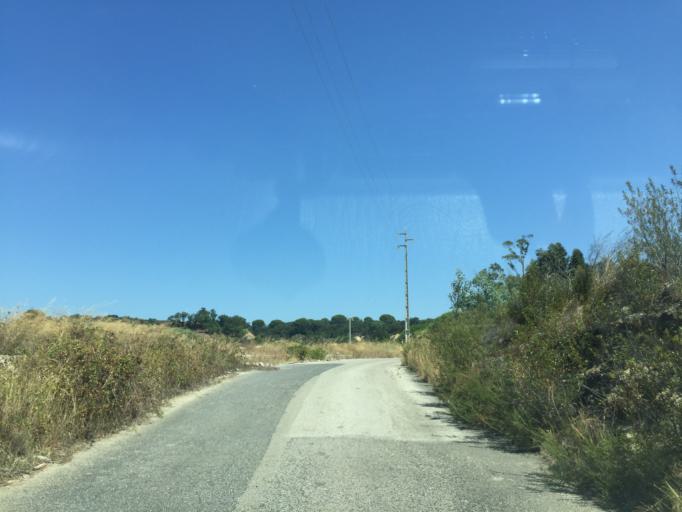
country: PT
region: Lisbon
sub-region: Alenquer
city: Carregado
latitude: 39.0464
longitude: -8.9284
